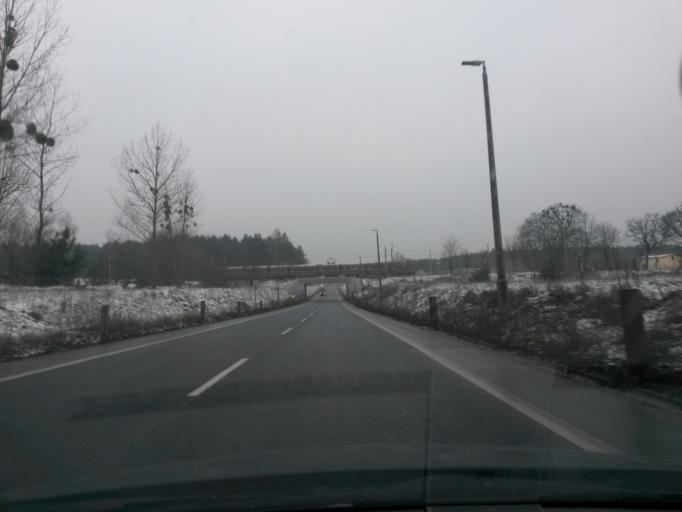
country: PL
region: Kujawsko-Pomorskie
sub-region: Powiat torunski
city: Wielka Nieszawka
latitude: 52.9758
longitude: 18.5565
